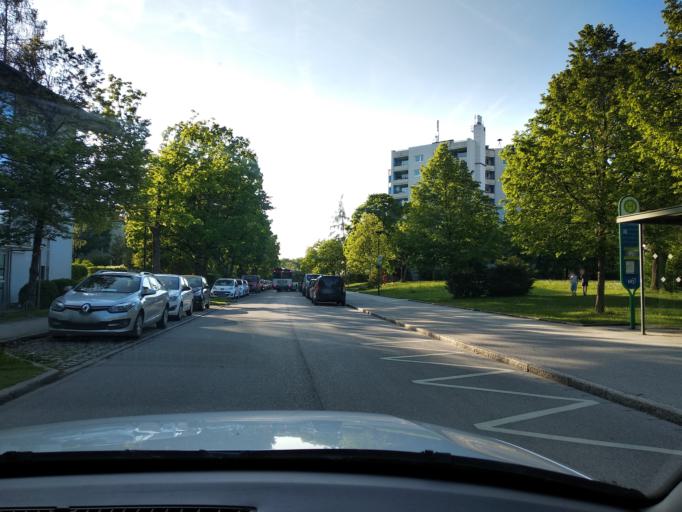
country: DE
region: Bavaria
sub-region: Upper Bavaria
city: Ottobrunn
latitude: 48.0681
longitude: 11.6863
